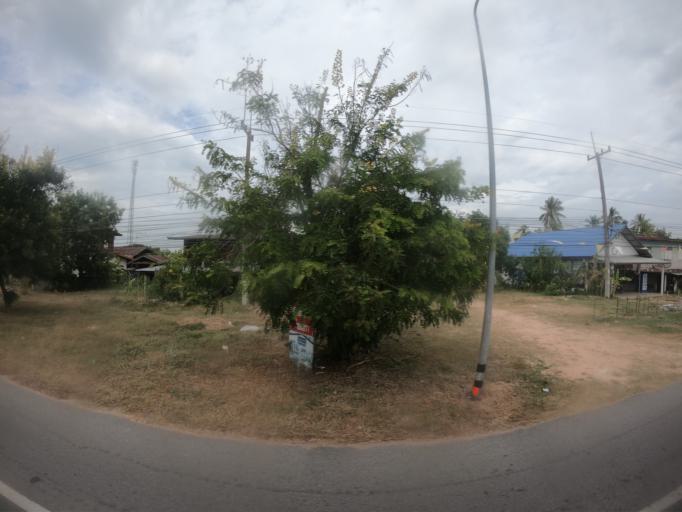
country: TH
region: Maha Sarakham
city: Maha Sarakham
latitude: 16.1488
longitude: 103.3972
